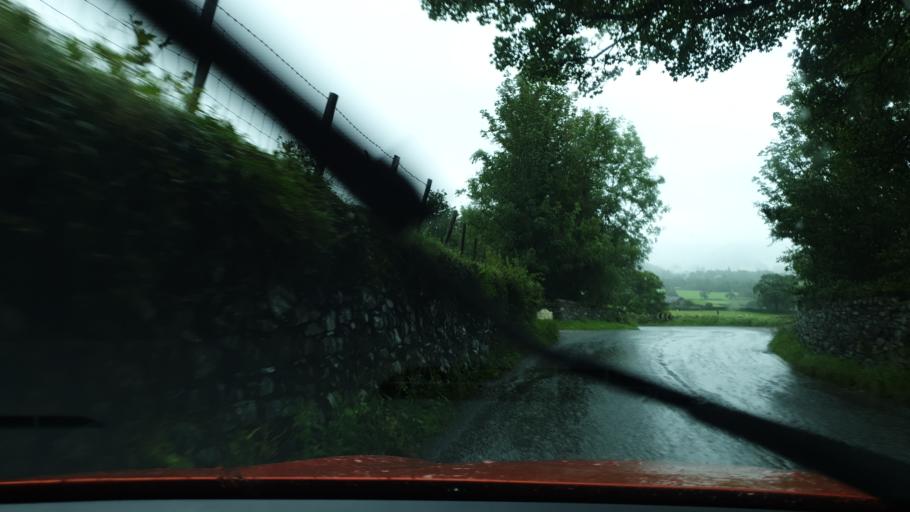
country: GB
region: England
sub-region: Cumbria
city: Ambleside
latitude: 54.3567
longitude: -3.0824
